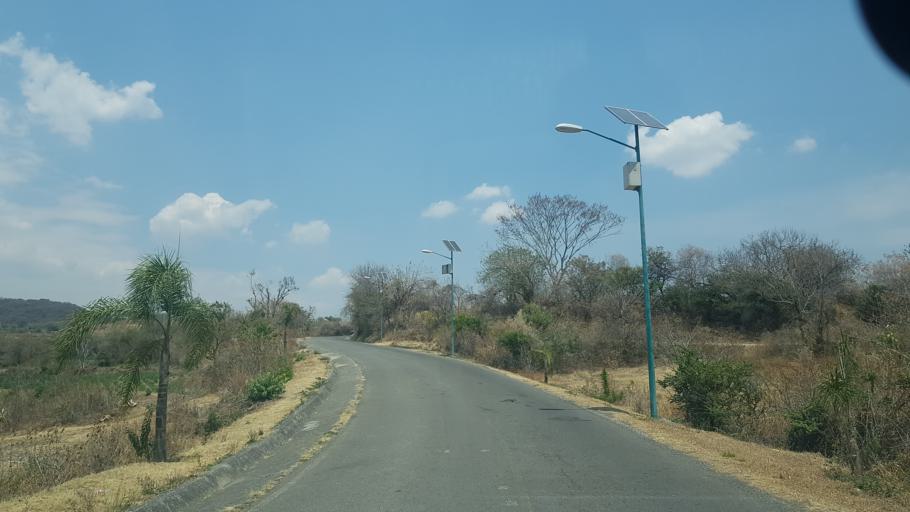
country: MX
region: Puebla
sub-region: Atzitzihuacan
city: Santiago Atzitzihuacan
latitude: 18.8355
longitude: -98.5776
